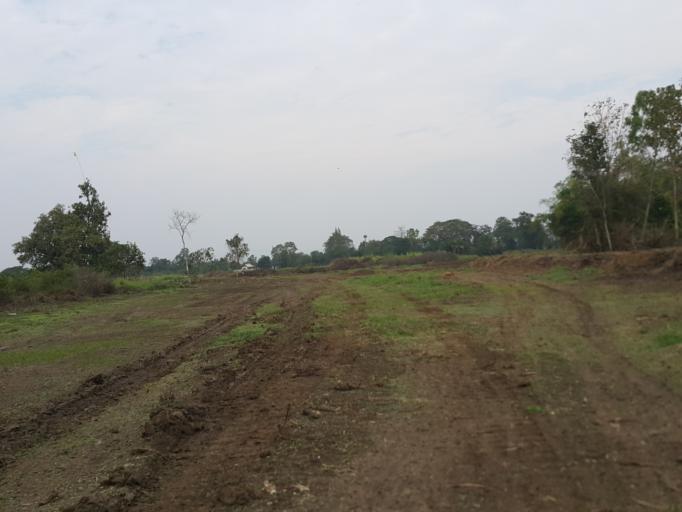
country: TH
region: Chiang Mai
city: San Kamphaeng
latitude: 18.7967
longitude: 99.1160
